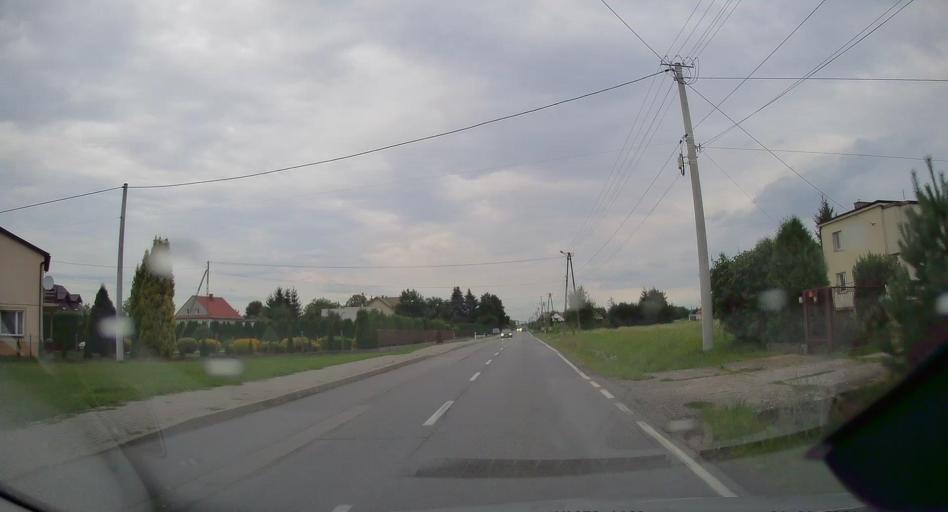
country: PL
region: Lesser Poland Voivodeship
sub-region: Powiat tarnowski
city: Wierzchoslawice
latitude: 50.0041
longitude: 20.8592
